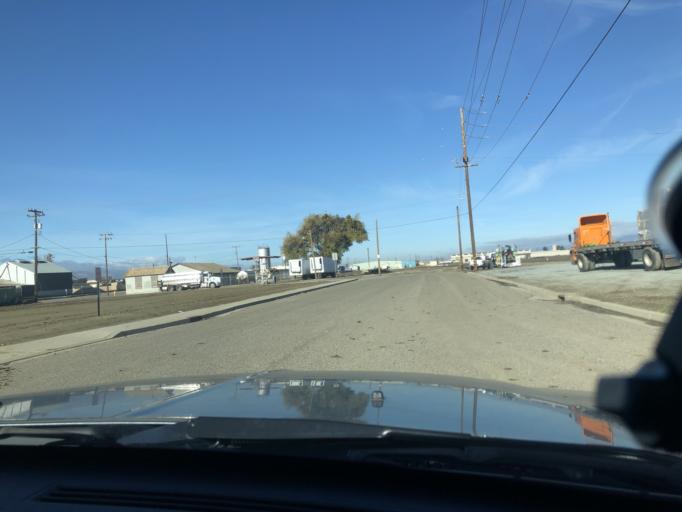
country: US
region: California
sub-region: Monterey County
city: King City
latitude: 36.2128
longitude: -121.1203
